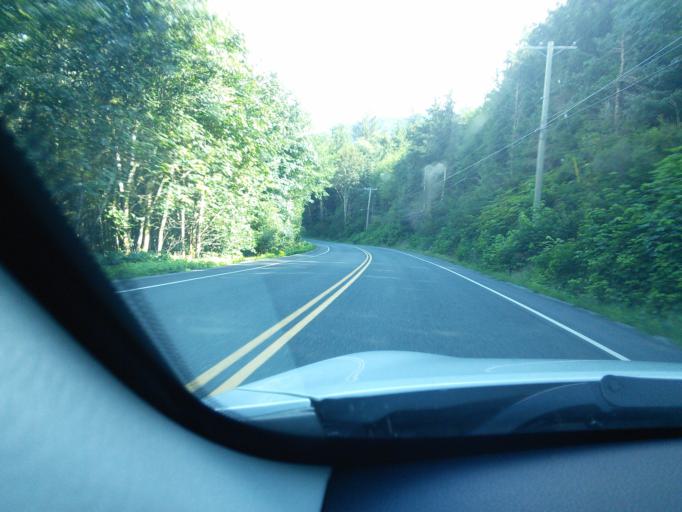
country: CA
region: British Columbia
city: Campbell River
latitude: 50.3485
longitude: -125.9055
